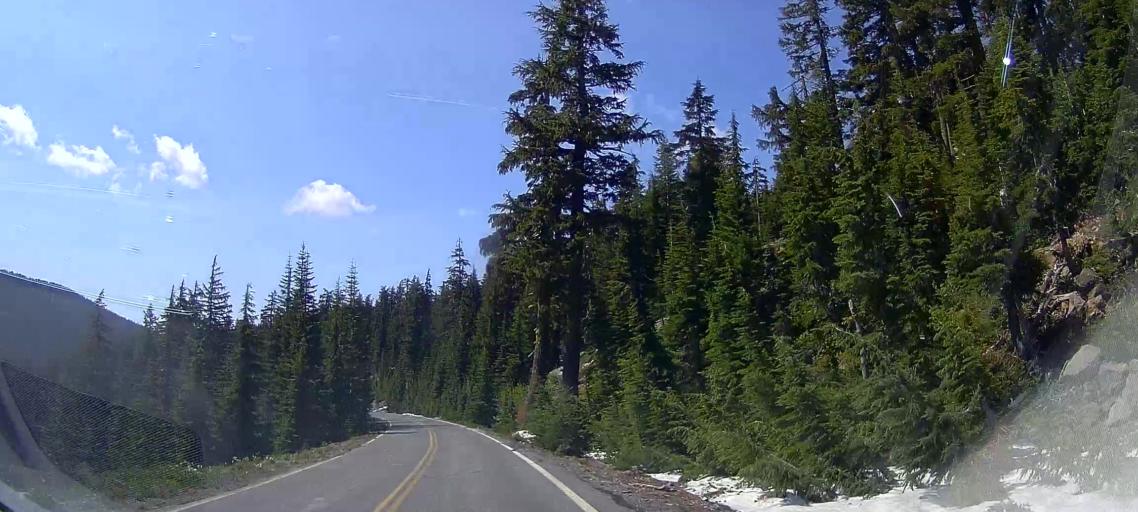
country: US
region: Oregon
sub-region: Klamath County
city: Klamath Falls
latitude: 42.8958
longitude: -122.0999
